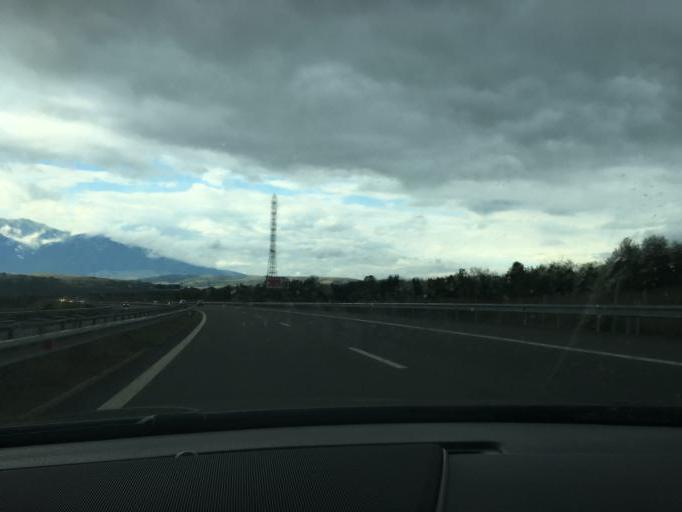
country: BG
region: Kyustendil
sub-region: Obshtina Dupnitsa
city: Dupnitsa
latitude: 42.3433
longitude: 23.0953
